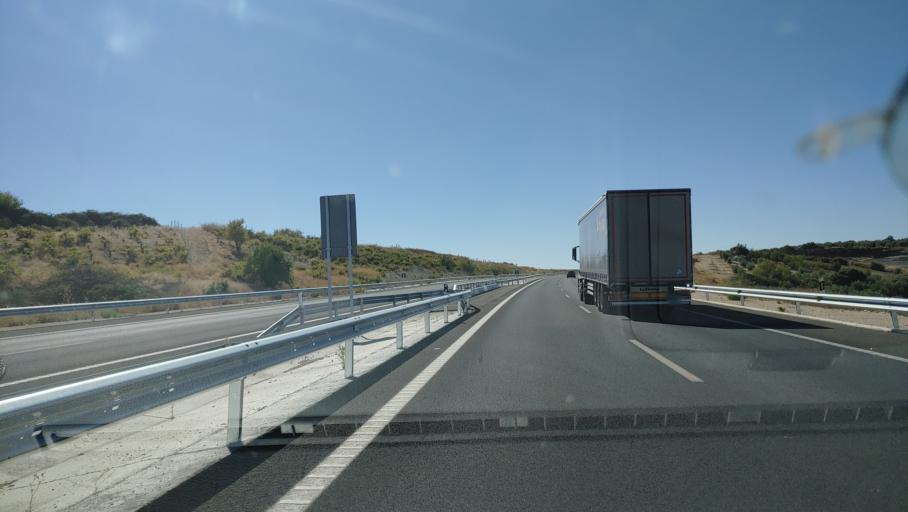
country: ES
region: Andalusia
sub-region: Provincia de Jaen
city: Torreperogil
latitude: 38.0418
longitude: -3.2645
